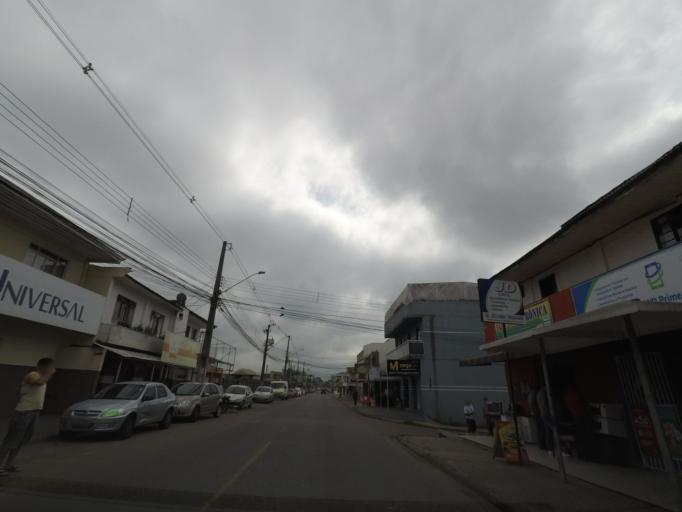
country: BR
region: Parana
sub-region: Curitiba
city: Curitiba
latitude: -25.5004
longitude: -49.3379
